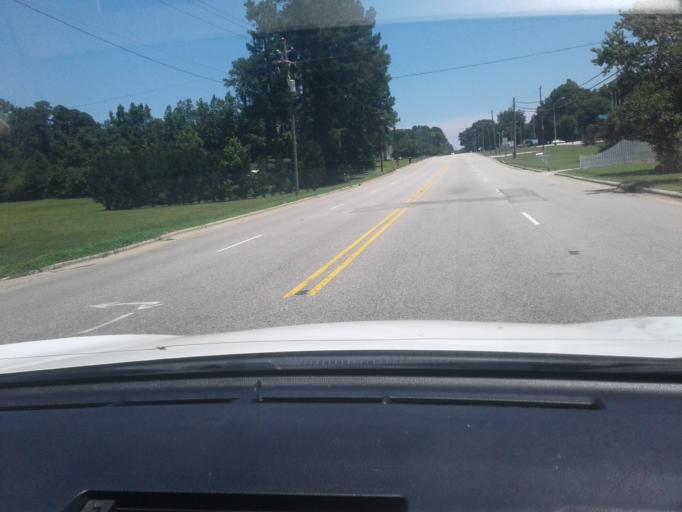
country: US
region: North Carolina
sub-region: Harnett County
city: Lillington
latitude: 35.3918
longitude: -78.8113
